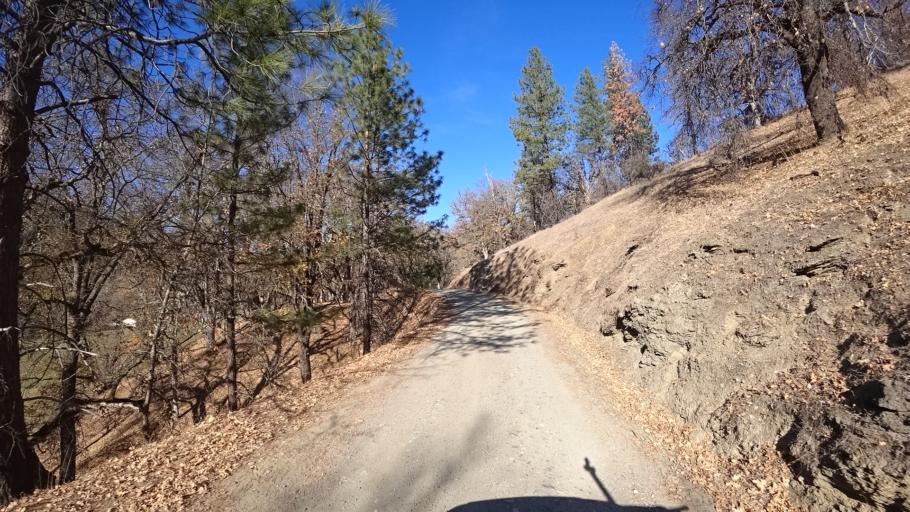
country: US
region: California
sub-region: Siskiyou County
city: Happy Camp
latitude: 41.8395
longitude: -123.0115
